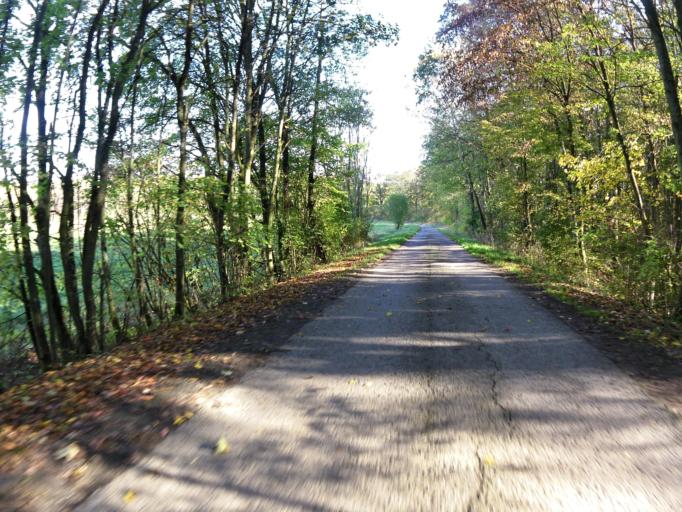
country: DE
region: Bavaria
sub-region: Regierungsbezirk Unterfranken
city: Sulzfeld am Main
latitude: 49.7187
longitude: 10.1047
